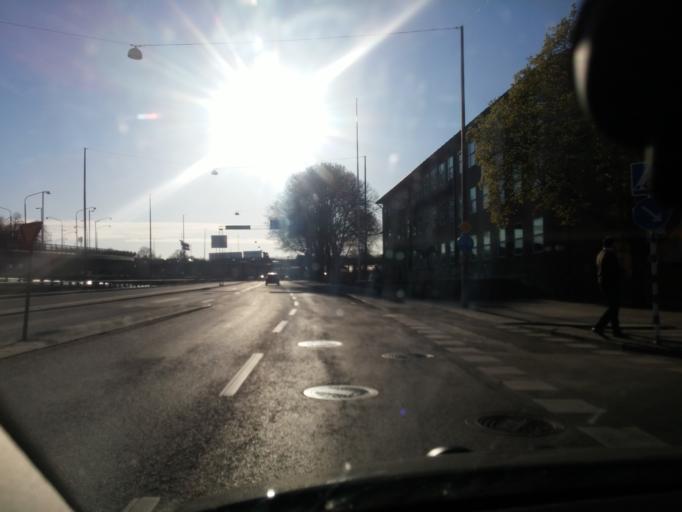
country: SE
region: Stockholm
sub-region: Solna Kommun
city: Solna
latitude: 59.3317
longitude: 18.0148
